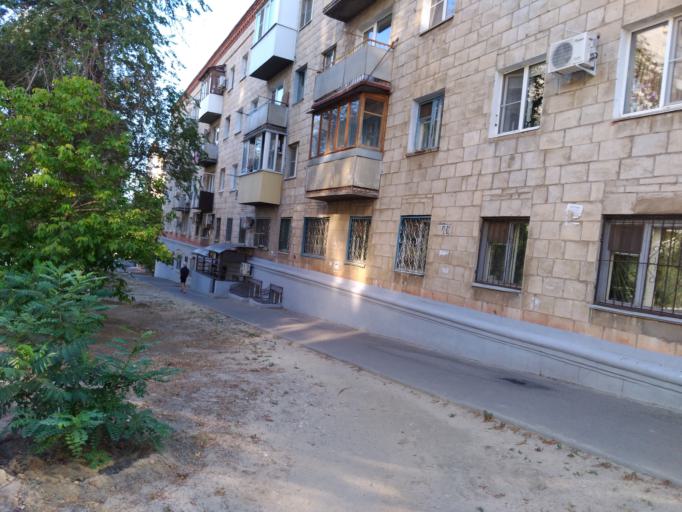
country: RU
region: Volgograd
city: Volgograd
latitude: 48.7182
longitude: 44.5164
